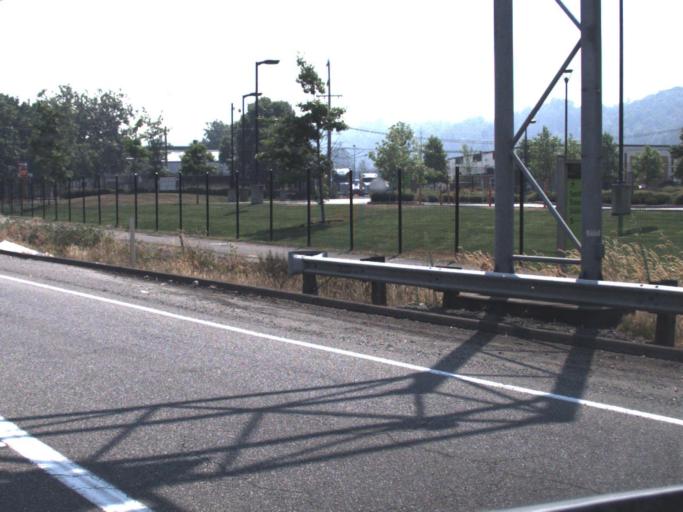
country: US
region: Washington
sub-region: King County
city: White Center
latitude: 47.5331
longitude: -122.3312
